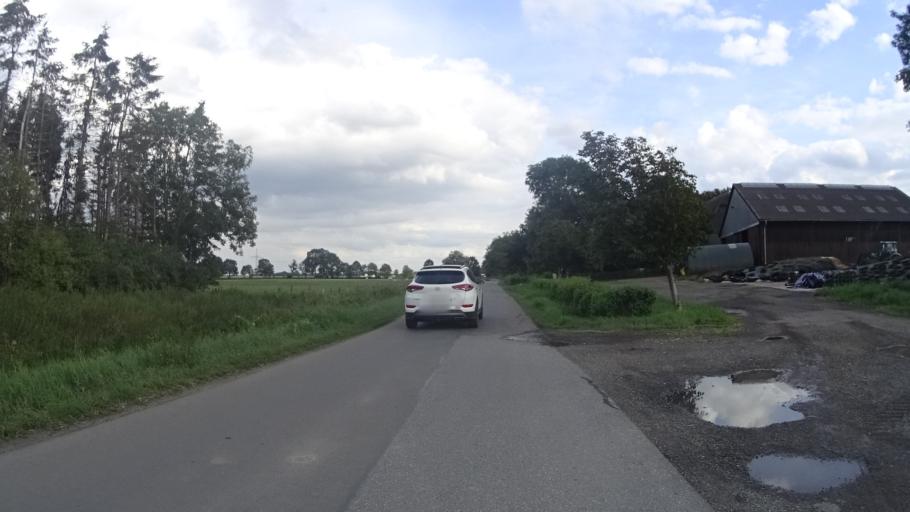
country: DE
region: Schleswig-Holstein
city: Herzhorn
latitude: 53.7741
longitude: 9.4861
